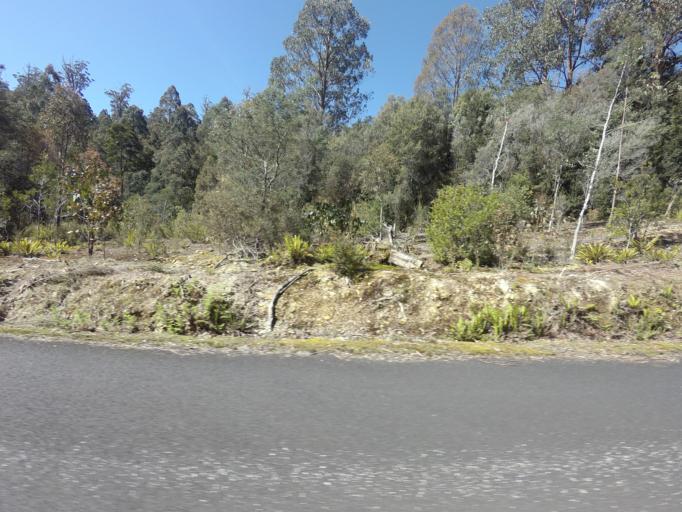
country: AU
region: Tasmania
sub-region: Huon Valley
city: Geeveston
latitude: -42.8199
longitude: 146.3317
